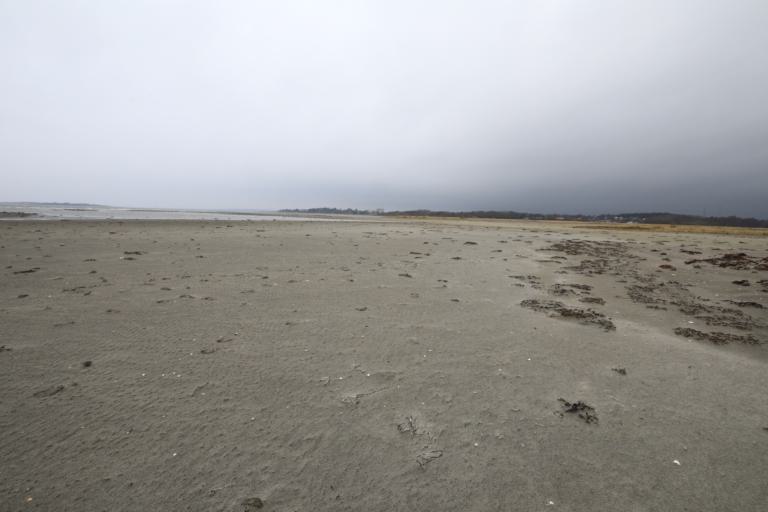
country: SE
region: Halland
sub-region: Kungsbacka Kommun
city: Frillesas
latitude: 57.3043
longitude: 12.1644
